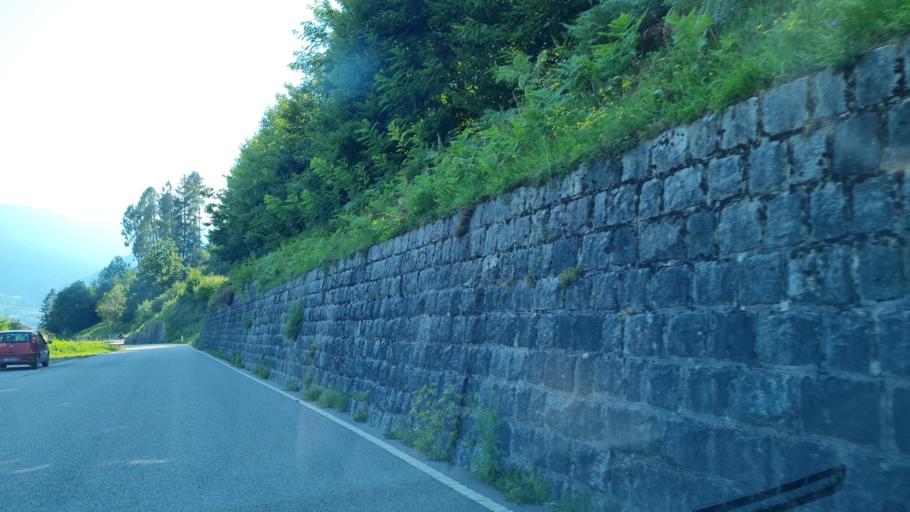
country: IT
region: Trentino-Alto Adige
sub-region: Provincia di Trento
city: Carzano
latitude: 46.0897
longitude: 11.4968
